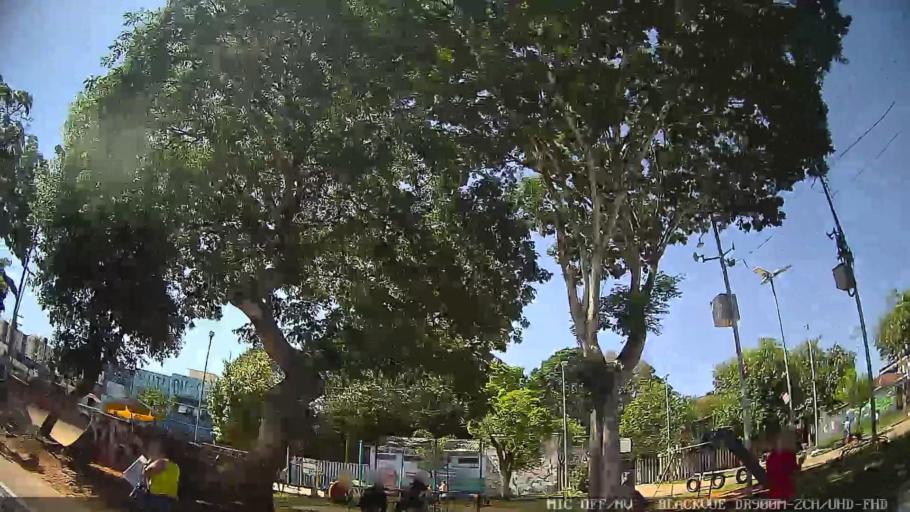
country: BR
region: Sao Paulo
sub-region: Sao Caetano Do Sul
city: Sao Caetano do Sul
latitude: -23.5990
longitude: -46.5159
